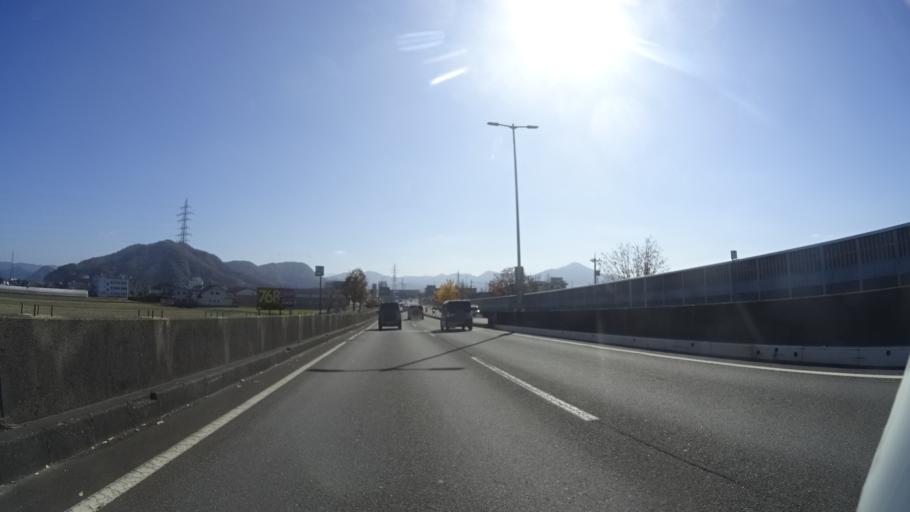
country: JP
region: Fukui
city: Sabae
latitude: 35.9521
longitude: 136.1914
